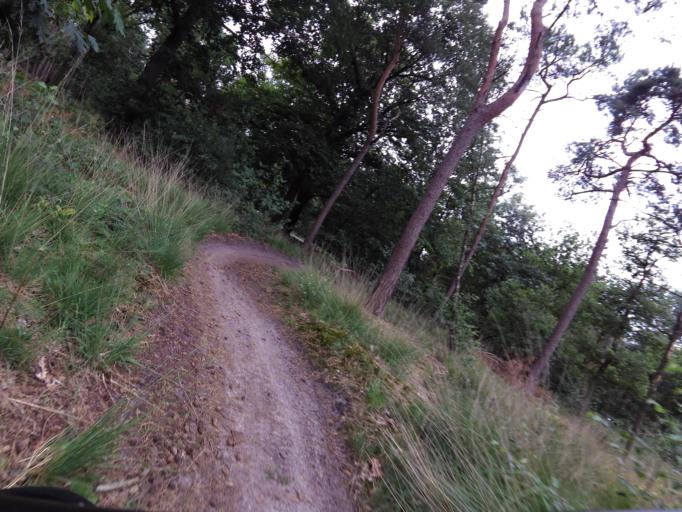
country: NL
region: North Brabant
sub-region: Gemeente Veghel
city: Keldonk
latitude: 51.5525
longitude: 5.5848
